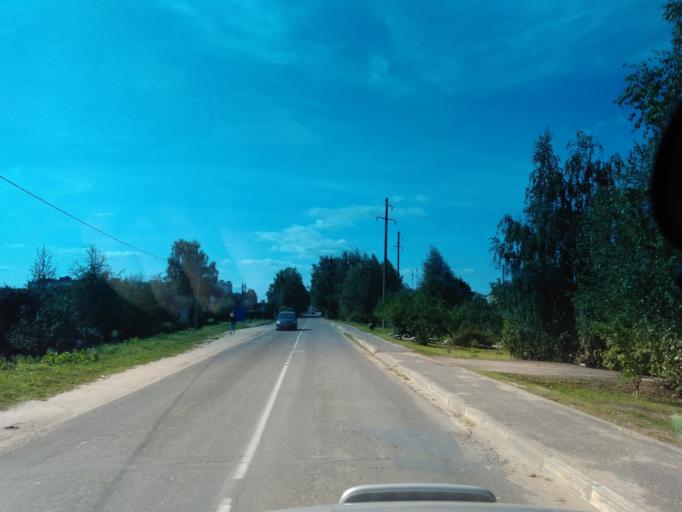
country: BY
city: Fanipol
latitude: 53.7490
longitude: 27.3378
